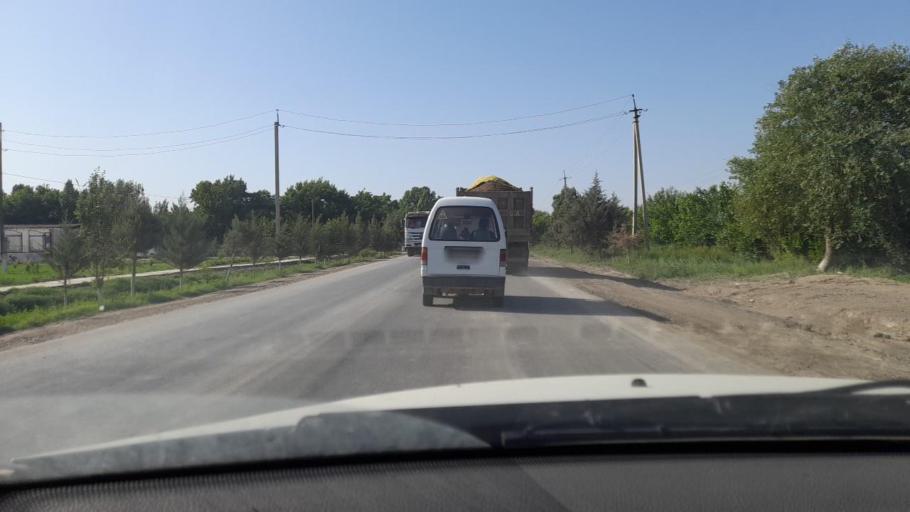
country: UZ
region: Bukhara
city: Romiton
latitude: 40.0503
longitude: 64.3285
